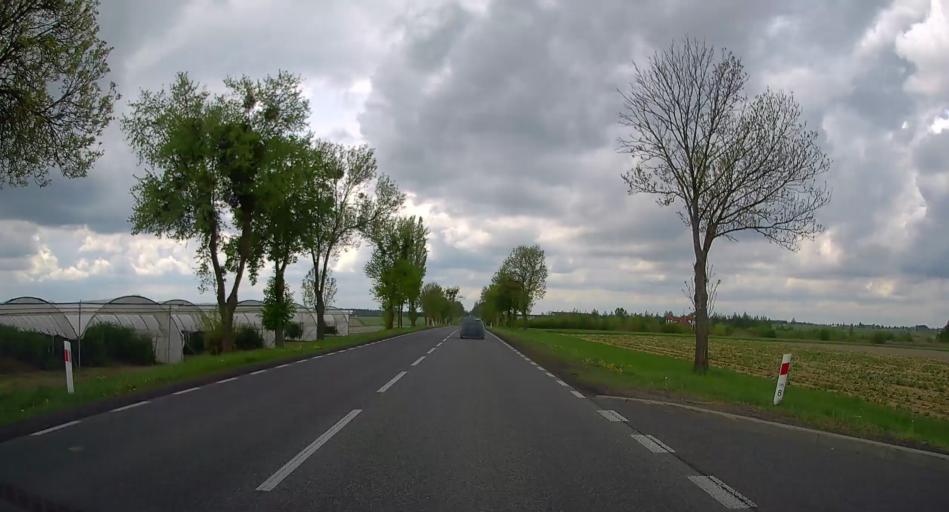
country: PL
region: Masovian Voivodeship
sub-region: Powiat plonski
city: Zaluski
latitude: 52.4399
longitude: 20.4834
